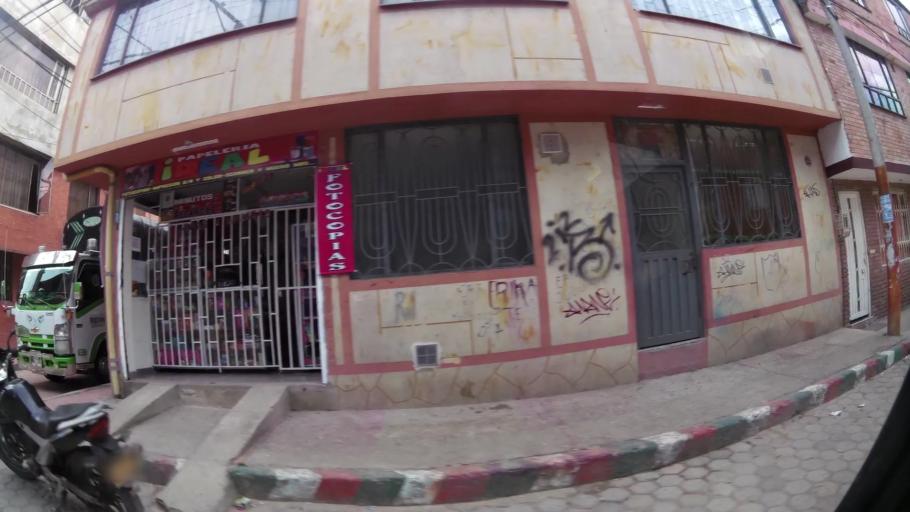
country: CO
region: Cundinamarca
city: Cota
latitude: 4.7279
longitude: -74.0976
